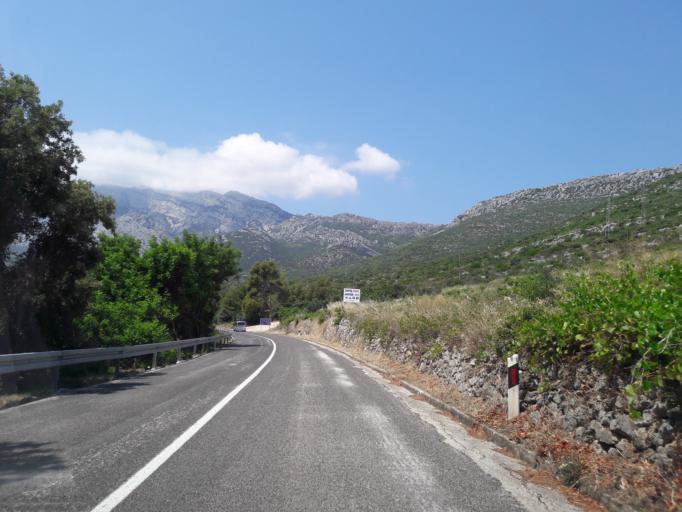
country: HR
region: Dubrovacko-Neretvanska
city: Orebic
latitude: 42.9805
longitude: 17.2203
